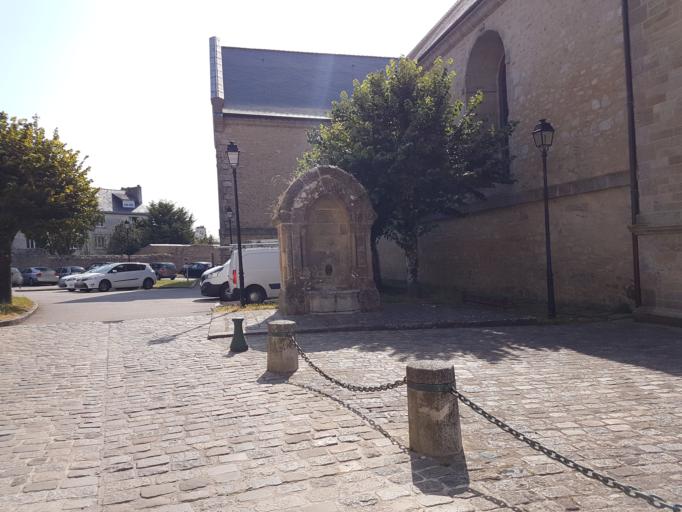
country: FR
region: Brittany
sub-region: Departement du Morbihan
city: Port-Louis
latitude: 47.7085
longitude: -3.3556
